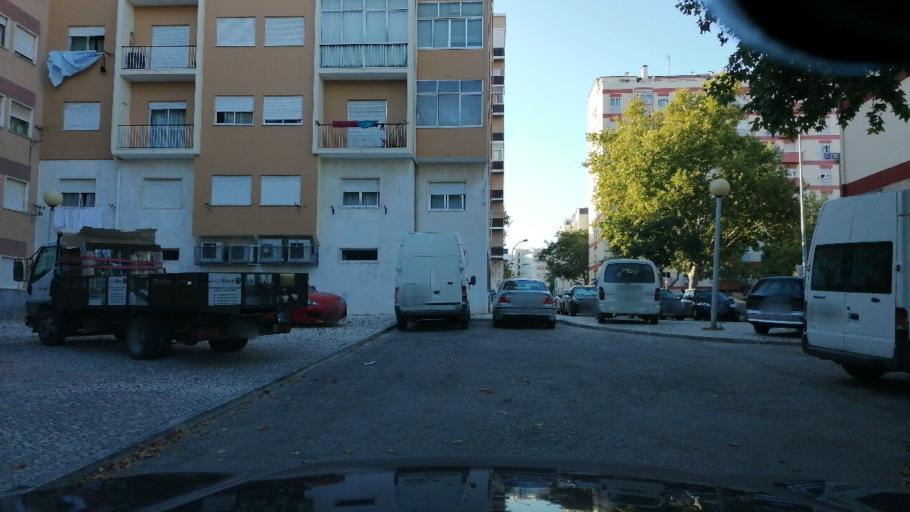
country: PT
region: Setubal
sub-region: Setubal
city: Setubal
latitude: 38.5368
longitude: -8.8924
